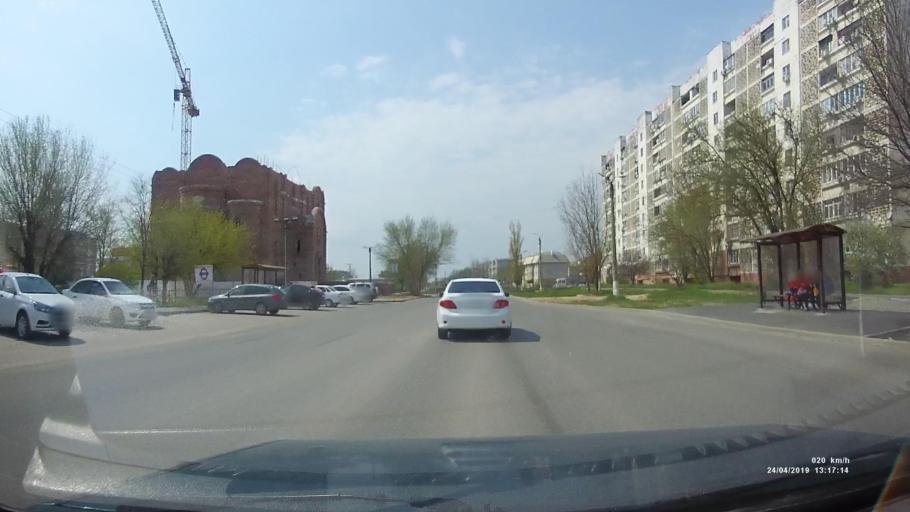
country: RU
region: Kalmykiya
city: Elista
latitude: 46.3052
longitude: 44.3009
